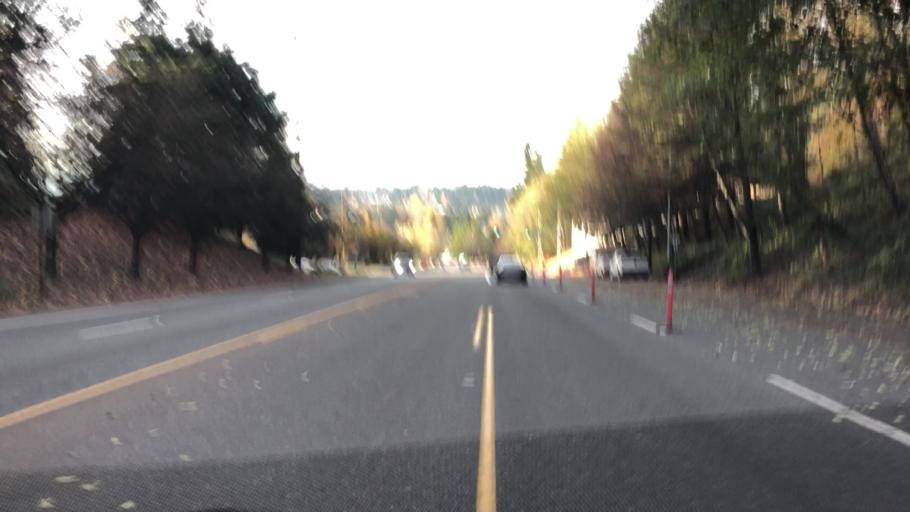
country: US
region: Washington
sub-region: King County
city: Woodinville
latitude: 47.7639
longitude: -122.1415
